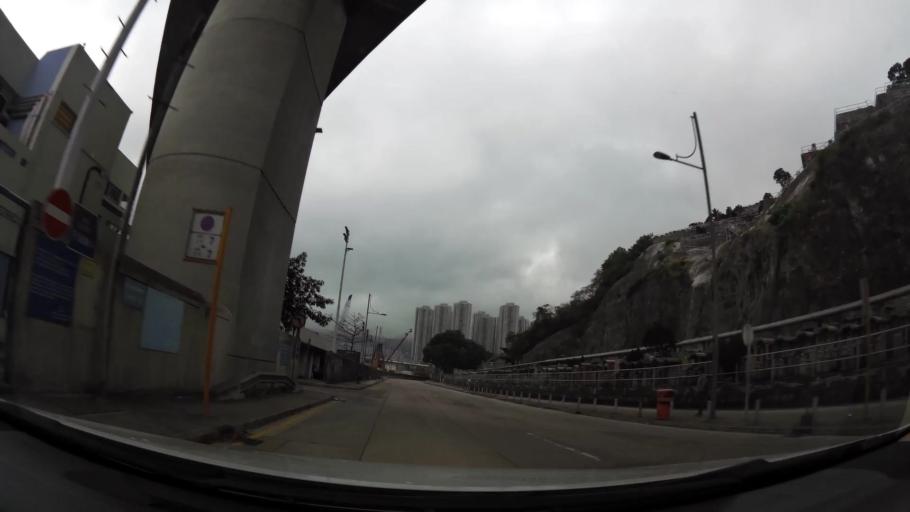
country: HK
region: Tsuen Wan
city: Tsuen Wan
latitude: 22.3557
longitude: 114.1159
